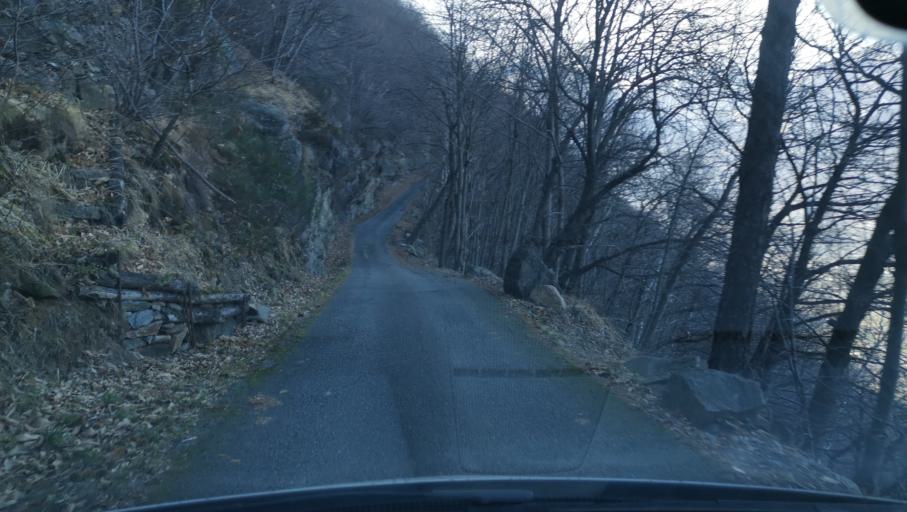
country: IT
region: Piedmont
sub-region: Provincia di Torino
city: Tavagnasco
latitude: 45.5386
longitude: 7.8151
